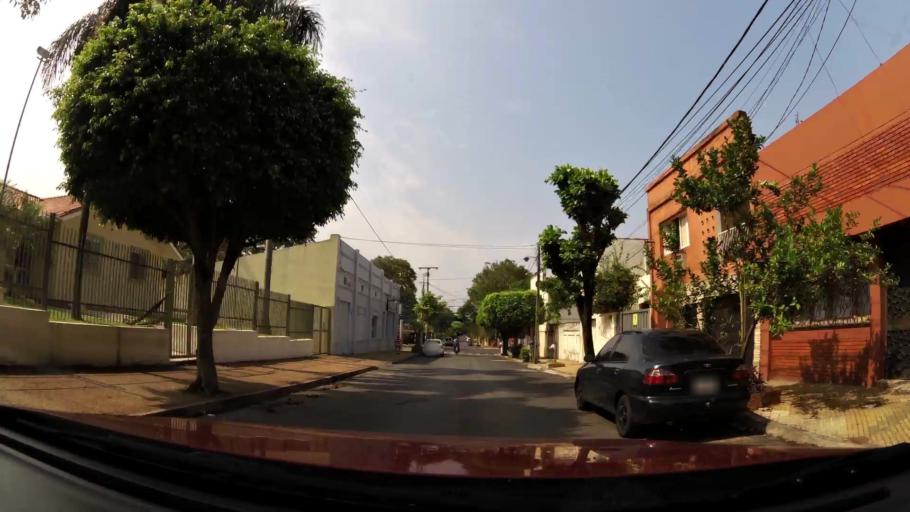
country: PY
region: Asuncion
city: Asuncion
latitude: -25.2885
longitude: -57.6562
